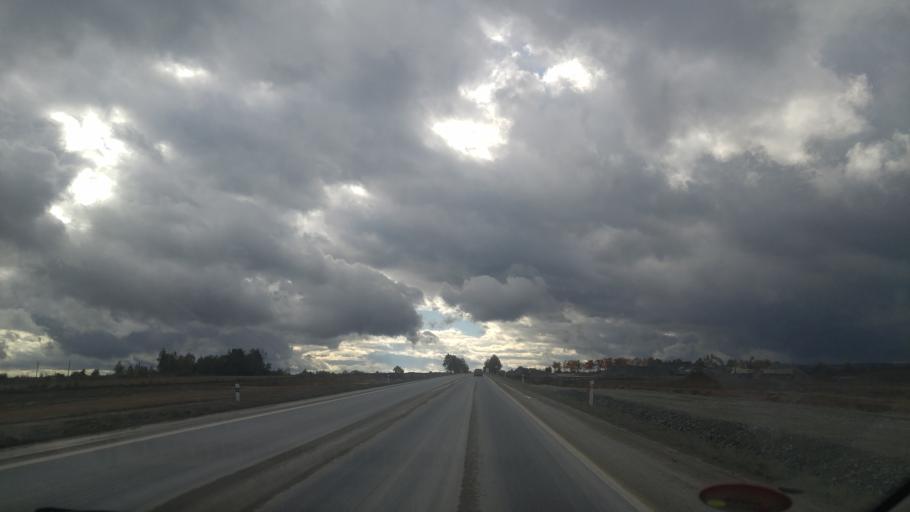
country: CZ
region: Jihocesky
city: Dolni Bukovsko
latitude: 49.1384
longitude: 14.6168
